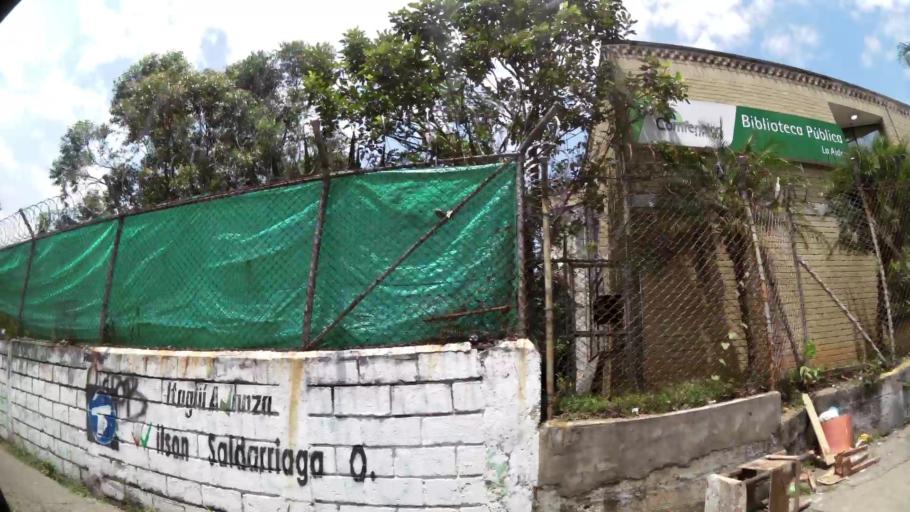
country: CO
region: Antioquia
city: Itagui
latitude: 6.1812
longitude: -75.6048
